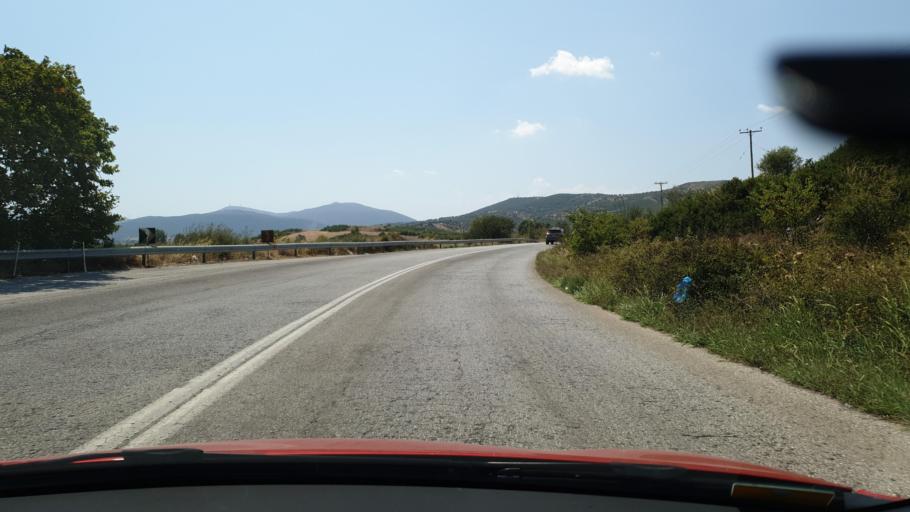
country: GR
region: Central Greece
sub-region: Nomos Evvoias
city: Aliveri
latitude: 38.4276
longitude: 24.1161
